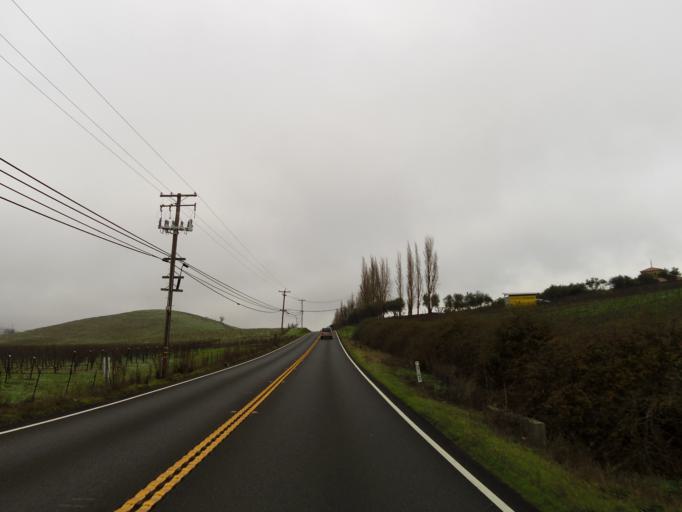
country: US
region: California
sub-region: Sonoma County
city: Temelec
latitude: 38.2066
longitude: -122.4521
